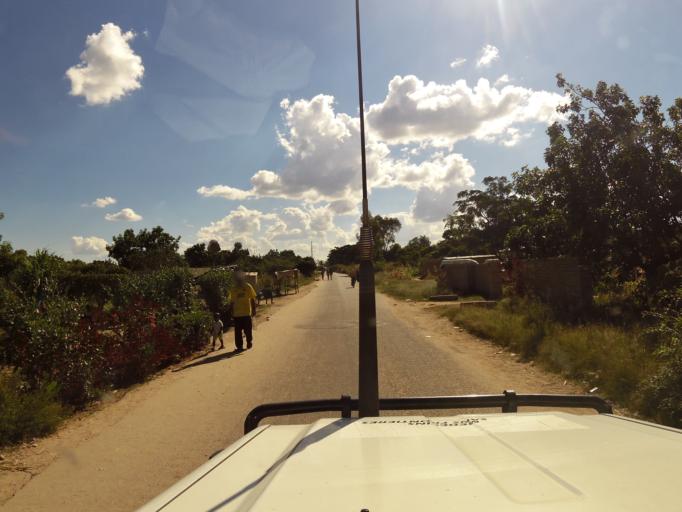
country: ZW
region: Harare
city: Epworth
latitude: -17.8749
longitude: 31.1412
